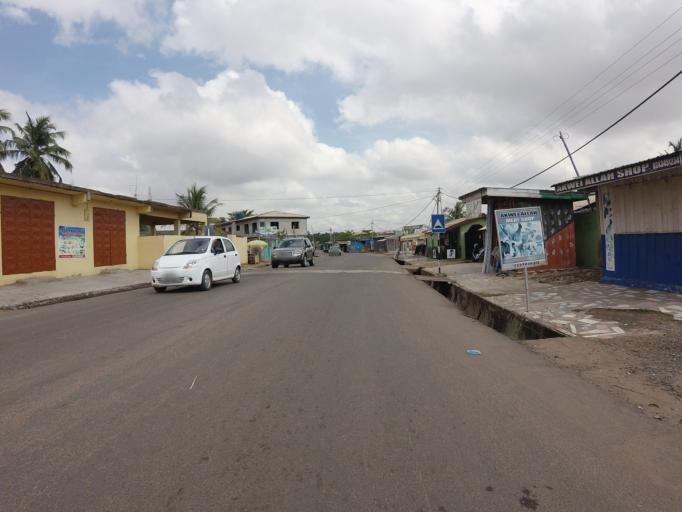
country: GH
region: Greater Accra
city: Nungua
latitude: 5.6160
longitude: -0.0851
